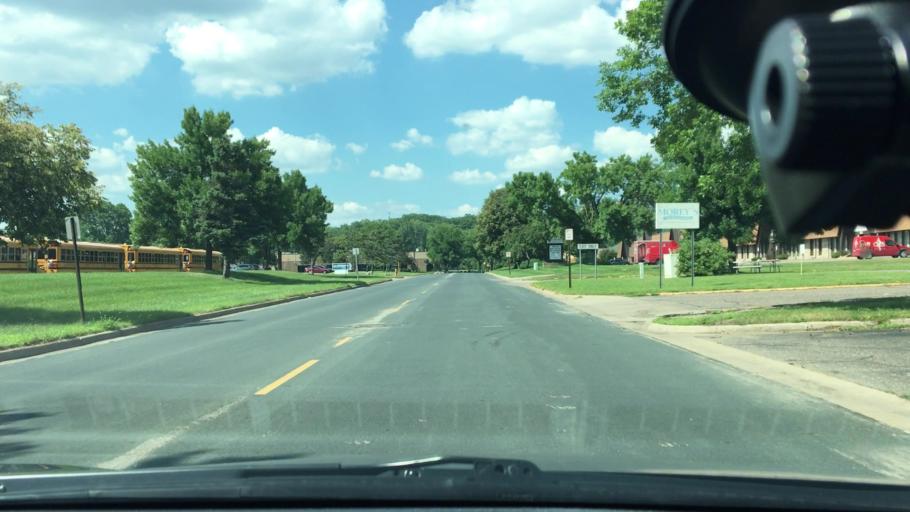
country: US
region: Minnesota
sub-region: Hennepin County
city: Golden Valley
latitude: 44.9869
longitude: -93.3928
